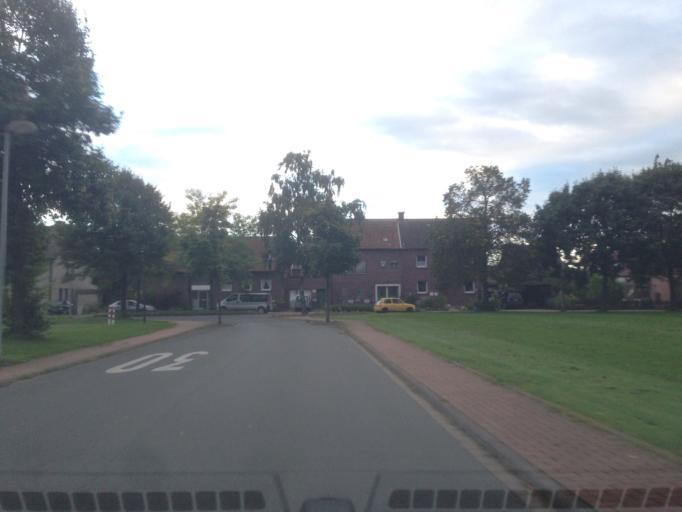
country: DE
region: North Rhine-Westphalia
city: Olfen
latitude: 51.7146
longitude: 7.3754
